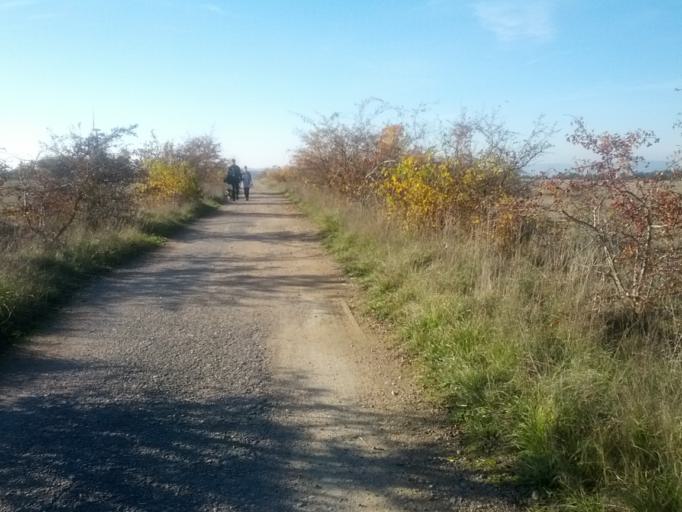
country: DE
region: Thuringia
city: Goldbach
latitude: 50.9592
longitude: 10.6405
